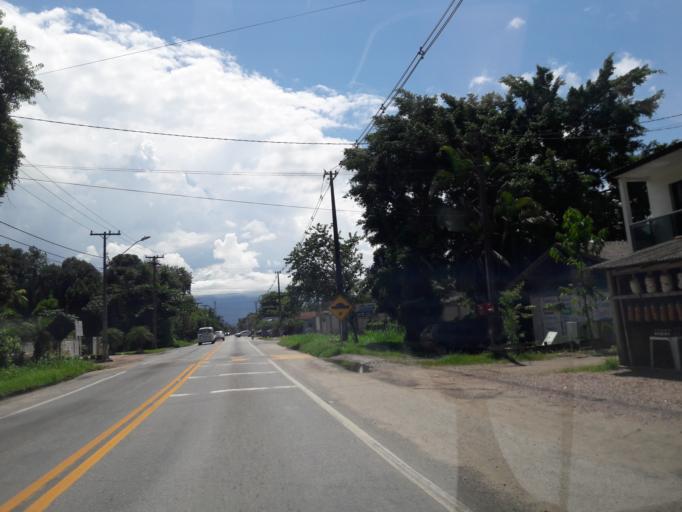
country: BR
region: Parana
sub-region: Antonina
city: Antonina
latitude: -25.4890
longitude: -48.8248
